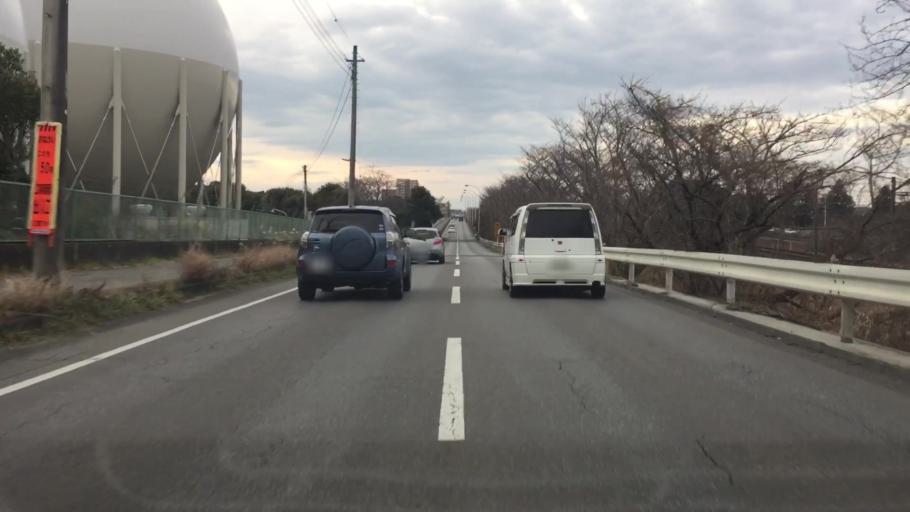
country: JP
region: Chiba
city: Shiroi
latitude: 35.7841
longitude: 140.0448
